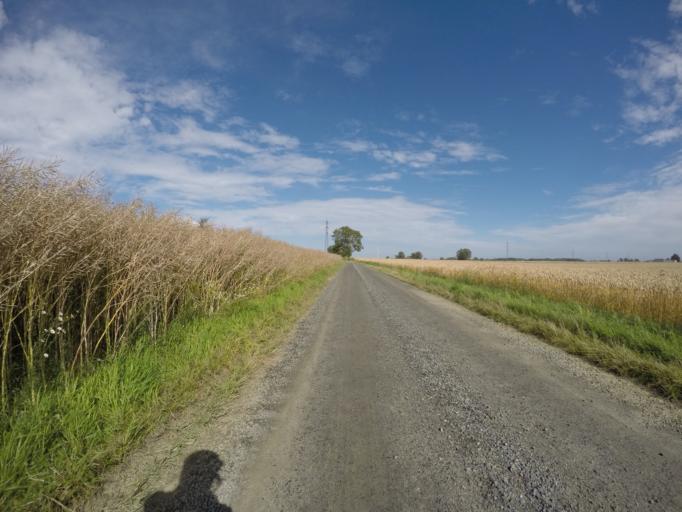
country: SE
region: Skane
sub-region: Tomelilla Kommun
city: Tomelilla
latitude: 55.4666
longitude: 14.1369
